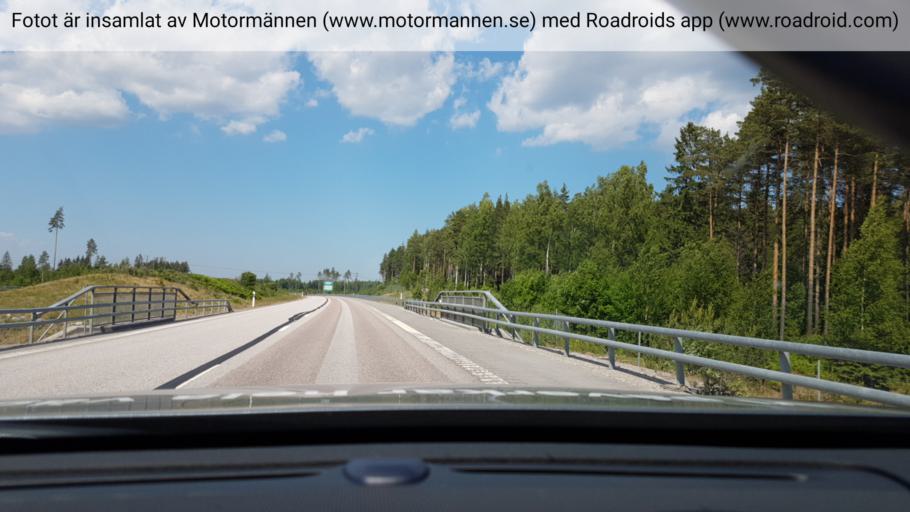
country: SE
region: Uppsala
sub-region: Tierps Kommun
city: Tierp
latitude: 60.3080
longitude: 17.5221
